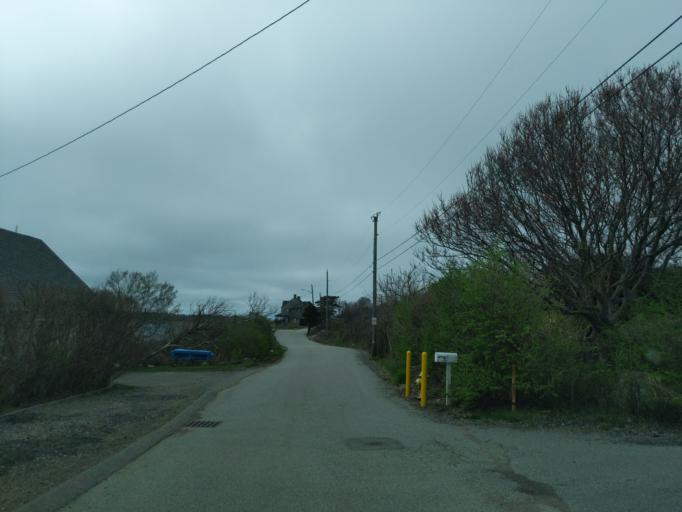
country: US
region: Massachusetts
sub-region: Essex County
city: Rockport
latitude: 42.6470
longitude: -70.5934
